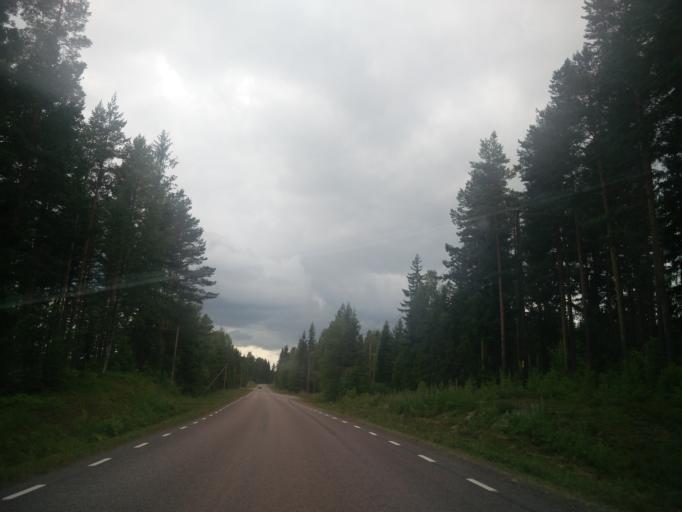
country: SE
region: Vaermland
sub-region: Arvika Kommun
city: Arvika
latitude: 59.9558
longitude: 12.7149
